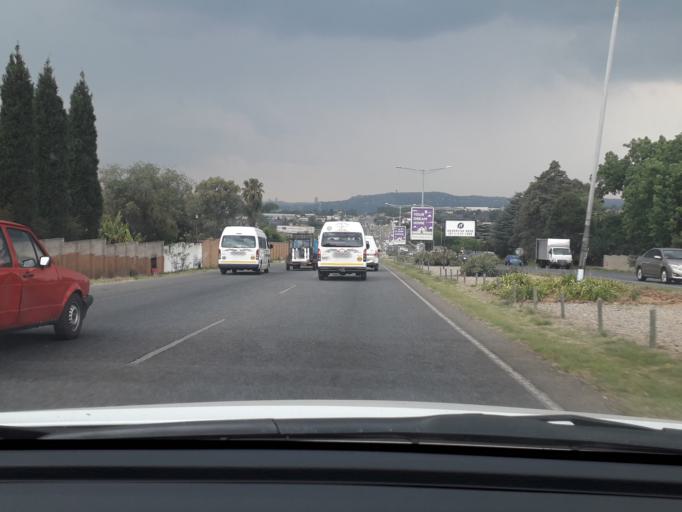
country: ZA
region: Gauteng
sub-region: City of Johannesburg Metropolitan Municipality
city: Roodepoort
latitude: -26.0844
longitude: 27.9337
